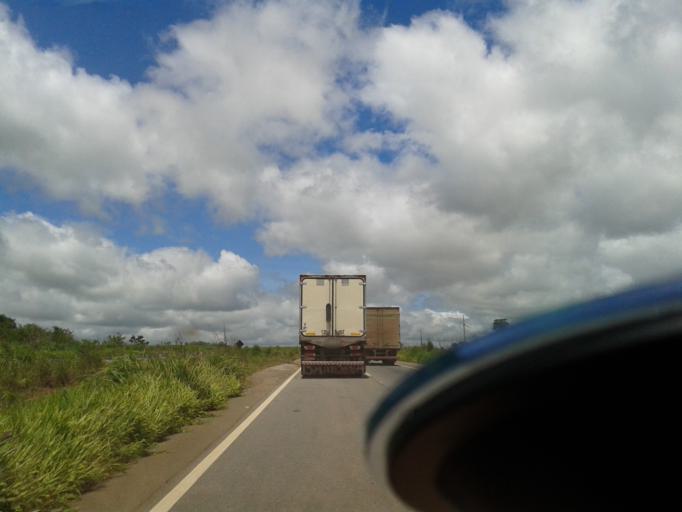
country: BR
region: Goias
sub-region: Itaberai
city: Itaberai
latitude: -16.0771
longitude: -49.7312
